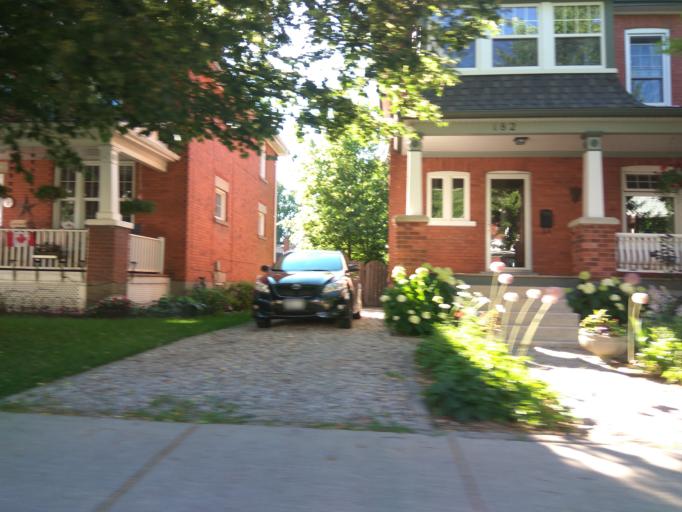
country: CA
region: Ontario
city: Stratford
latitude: 43.3757
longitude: -80.9909
